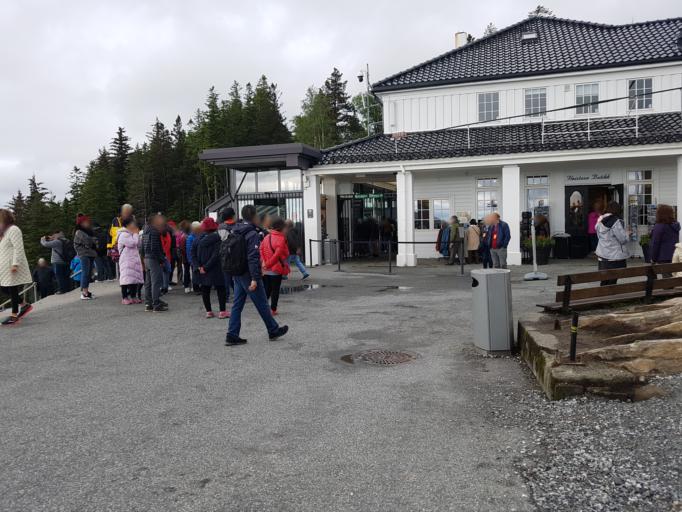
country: NO
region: Hordaland
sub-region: Bergen
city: Bergen
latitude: 60.3944
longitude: 5.3431
